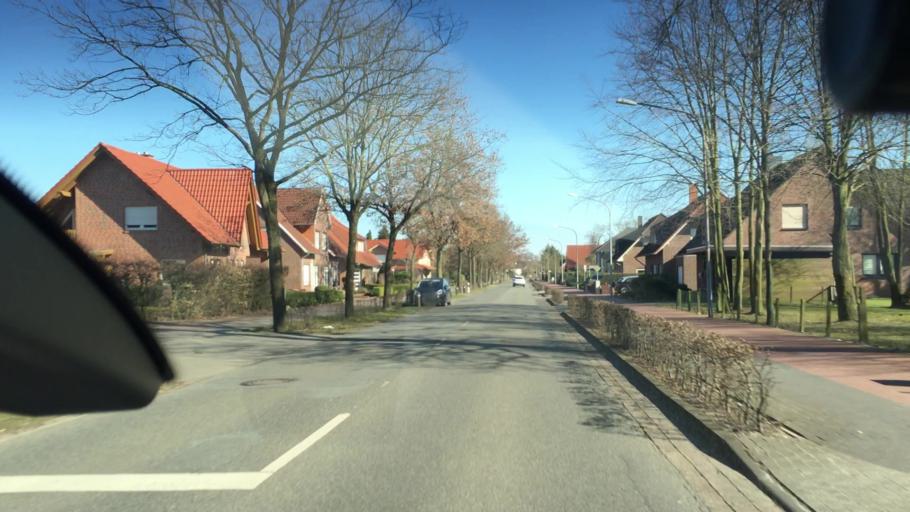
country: DE
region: Lower Saxony
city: Lohne
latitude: 52.6712
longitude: 8.2200
